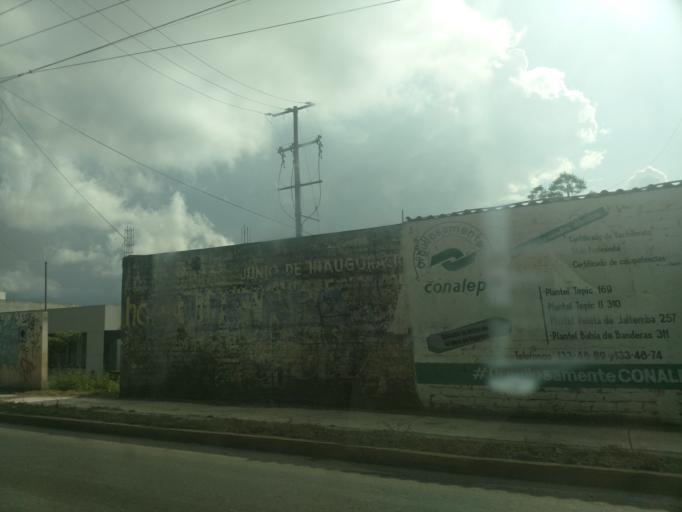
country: MX
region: Nayarit
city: Tepic
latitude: 21.4944
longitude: -104.8680
